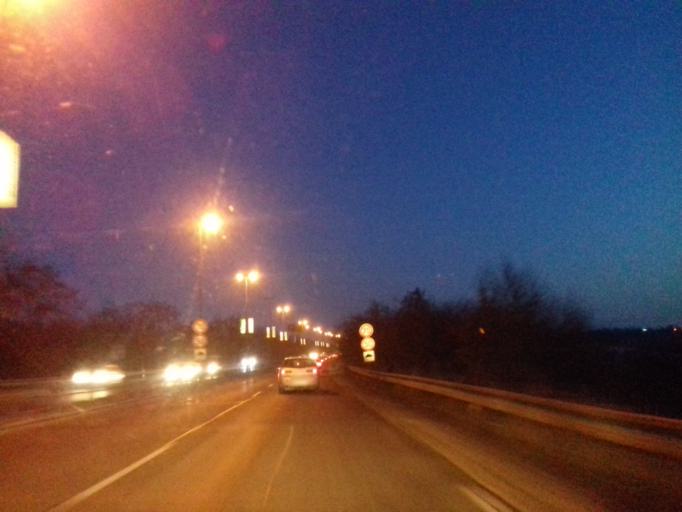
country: CZ
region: Central Bohemia
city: Tuchomerice
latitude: 50.1129
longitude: 14.2878
